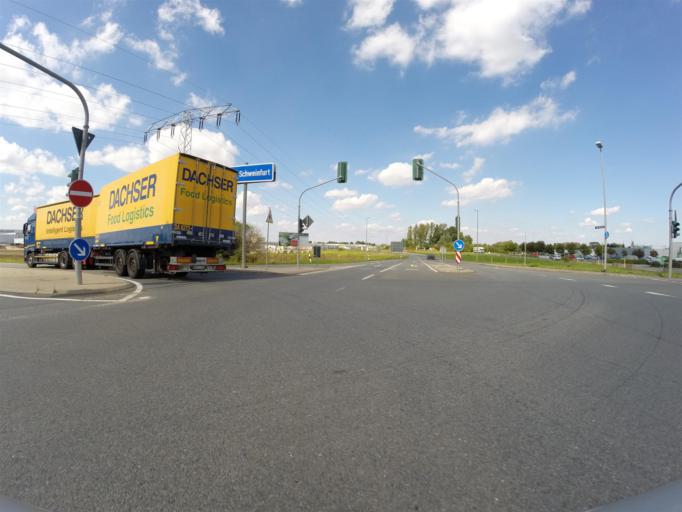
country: DE
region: Thuringia
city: Noda
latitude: 51.0336
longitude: 11.0010
